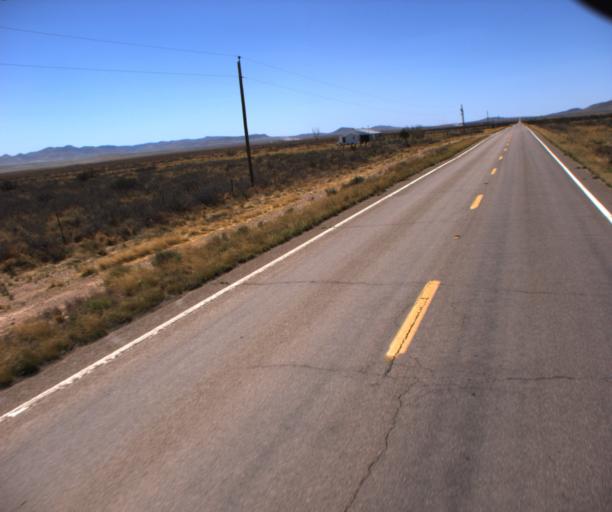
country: US
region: Arizona
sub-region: Cochise County
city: Douglas
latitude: 31.7504
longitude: -109.0912
